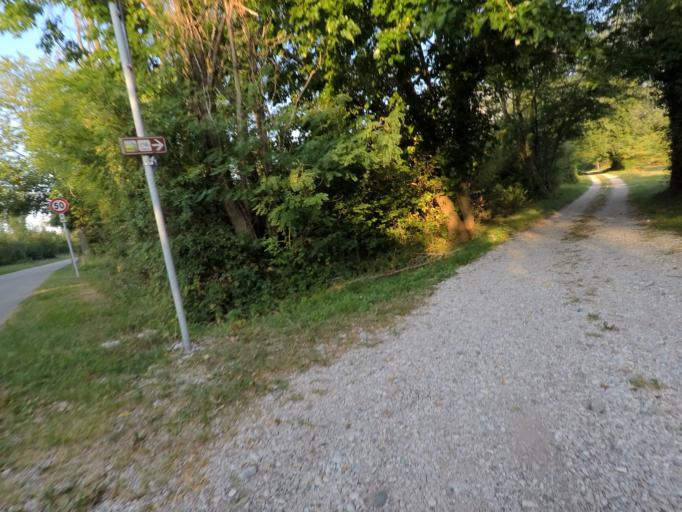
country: IT
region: Friuli Venezia Giulia
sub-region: Provincia di Udine
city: Trasaghis
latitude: 46.2791
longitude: 13.0800
